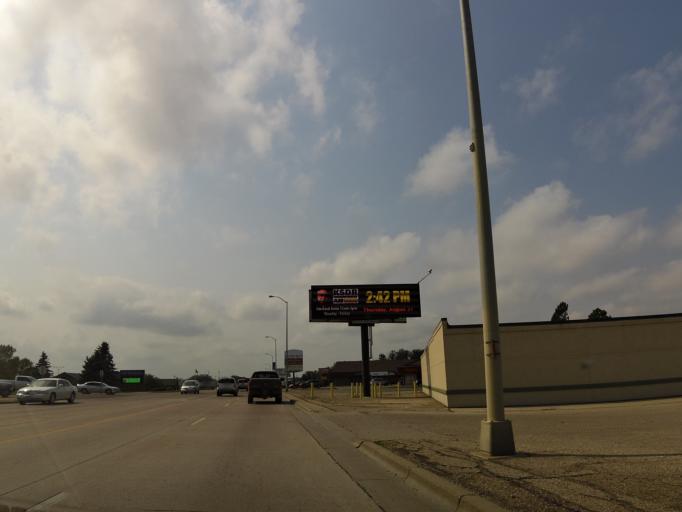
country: US
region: South Dakota
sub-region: Codington County
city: Watertown
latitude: 44.8901
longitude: -97.0921
